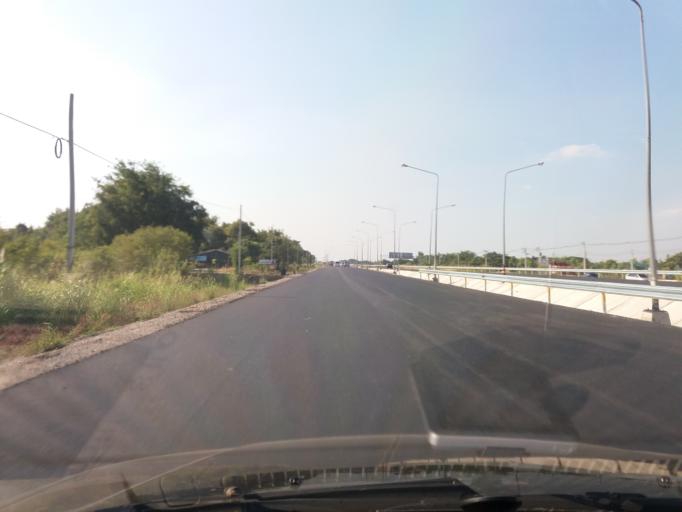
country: TH
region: Nakhon Sawan
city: Krok Phra
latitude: 15.6214
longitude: 100.1146
